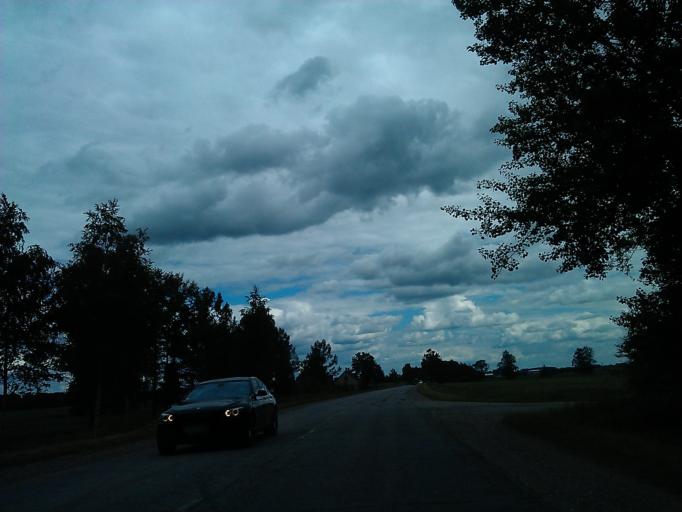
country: LV
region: Dobeles Rajons
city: Dobele
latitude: 56.6199
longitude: 23.3786
